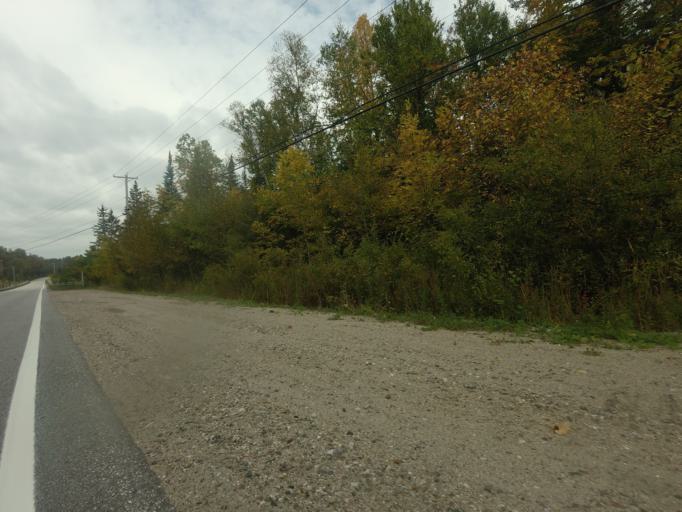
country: CA
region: Quebec
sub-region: Outaouais
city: Wakefield
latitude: 45.9324
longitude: -75.9864
